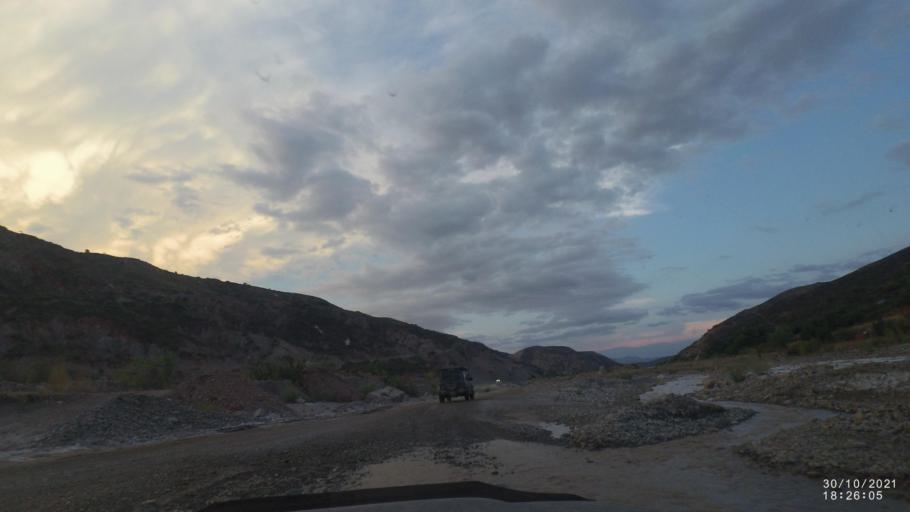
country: BO
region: Cochabamba
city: Sipe Sipe
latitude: -17.5506
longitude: -66.3968
